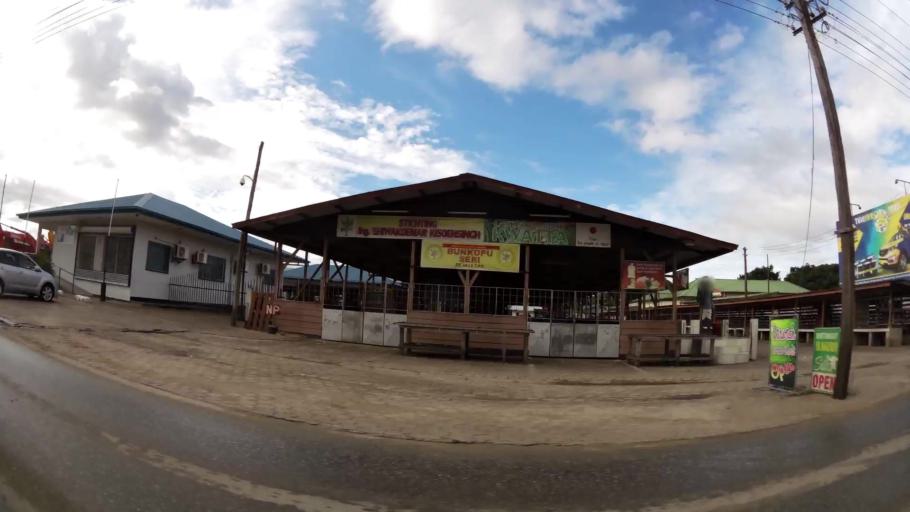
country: SR
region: Paramaribo
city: Paramaribo
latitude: 5.8464
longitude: -55.2301
